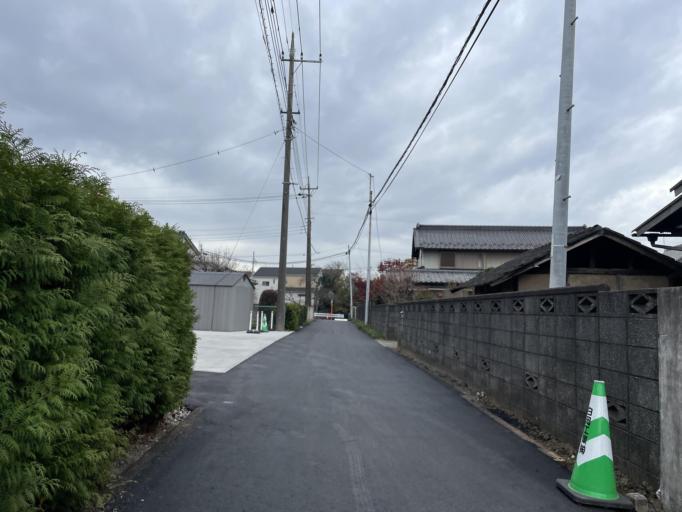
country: JP
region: Saitama
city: Shiraoka
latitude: 36.0322
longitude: 139.6550
